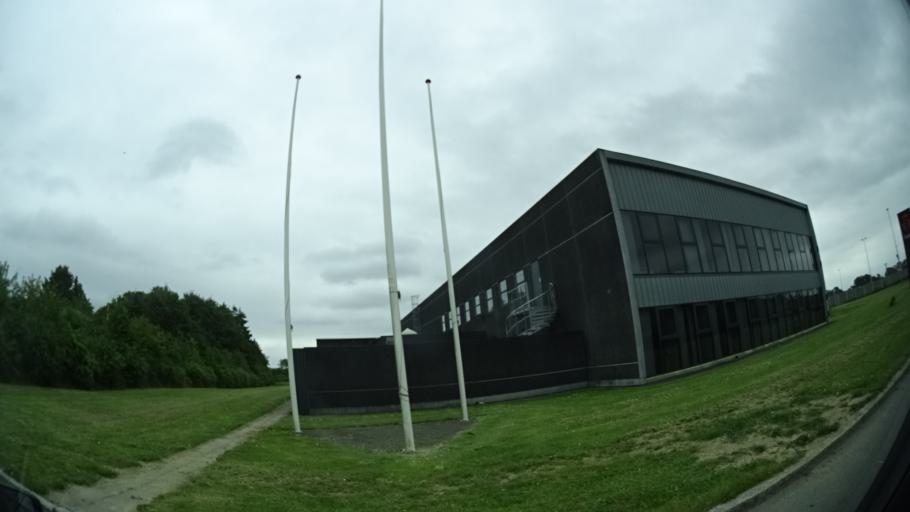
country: DK
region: Central Jutland
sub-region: Arhus Kommune
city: Kolt
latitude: 56.1008
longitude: 10.0705
